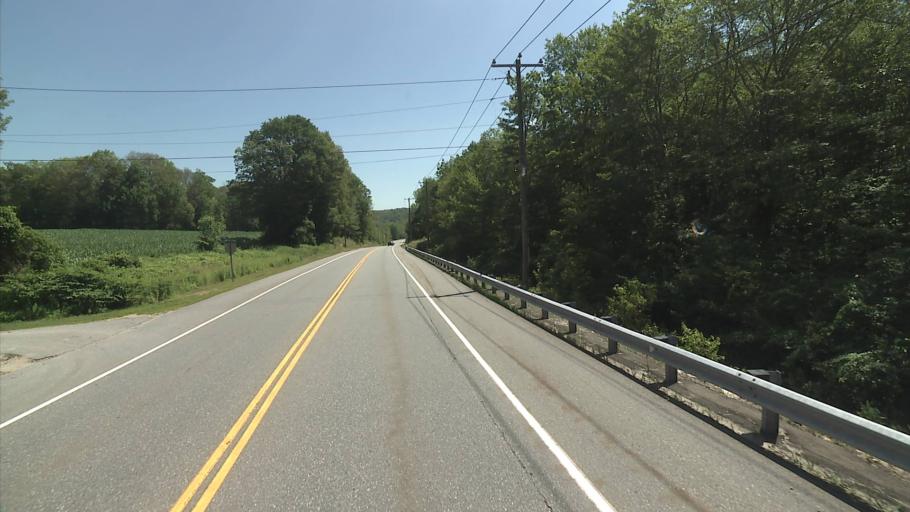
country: US
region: Connecticut
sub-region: Windham County
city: Moosup
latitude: 41.6806
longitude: -71.8718
